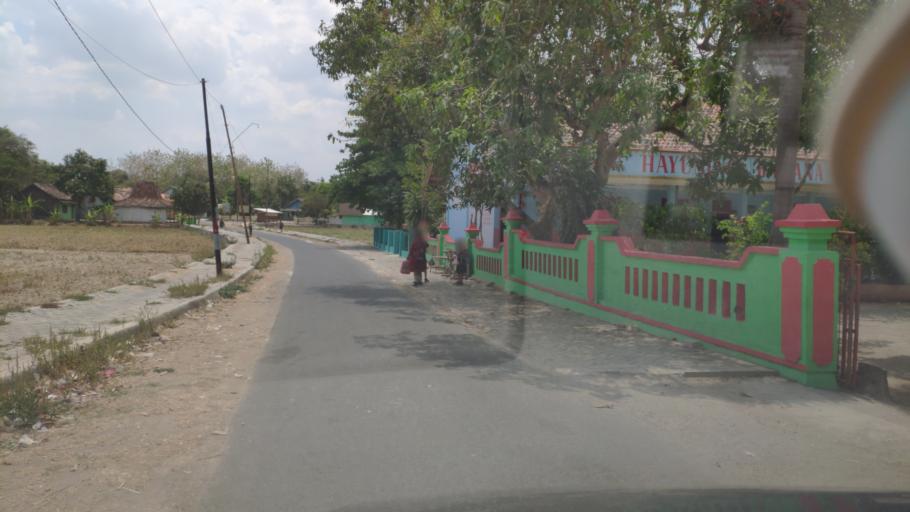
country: ID
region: Central Java
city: Tambaksari Satu
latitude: -6.9352
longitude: 111.4353
